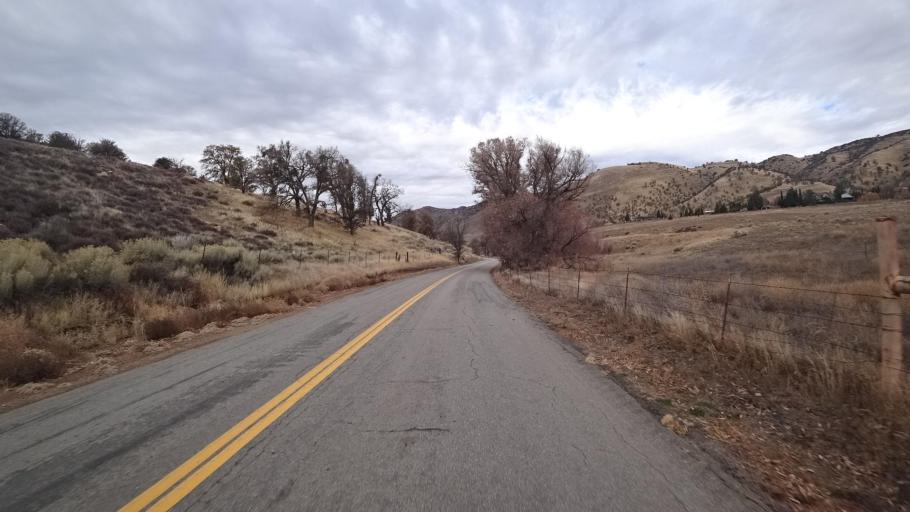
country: US
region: California
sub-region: Kern County
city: Golden Hills
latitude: 35.1244
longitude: -118.5540
